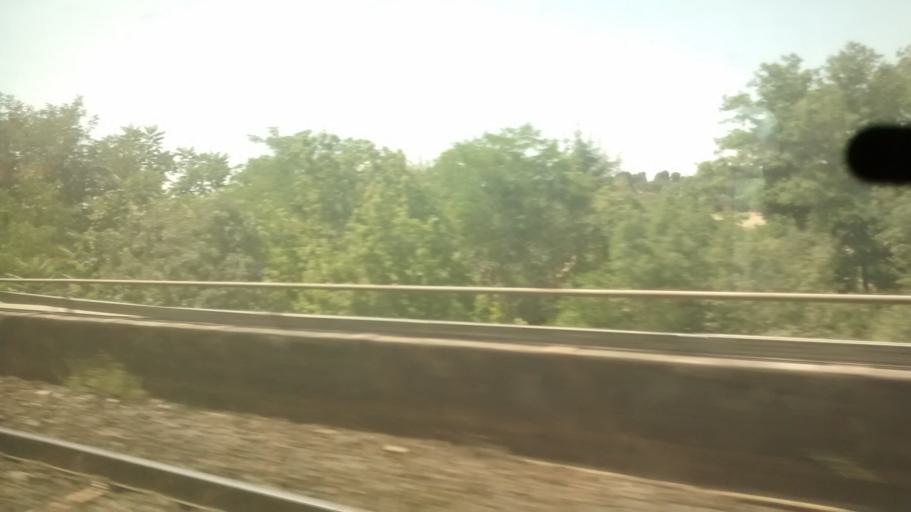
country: FR
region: Languedoc-Roussillon
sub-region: Departement du Gard
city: Gallargues-le-Montueux
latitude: 43.7089
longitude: 4.1611
